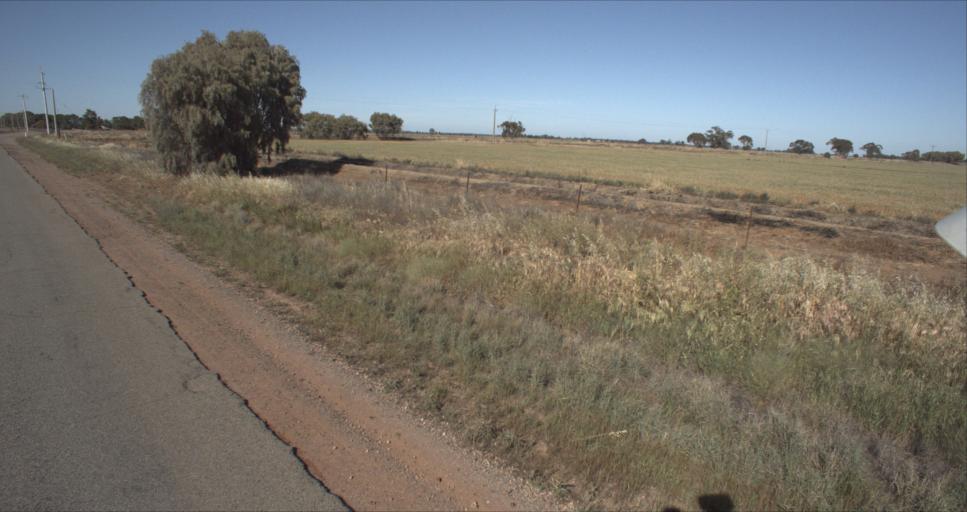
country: AU
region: New South Wales
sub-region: Leeton
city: Leeton
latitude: -34.5657
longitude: 146.3119
